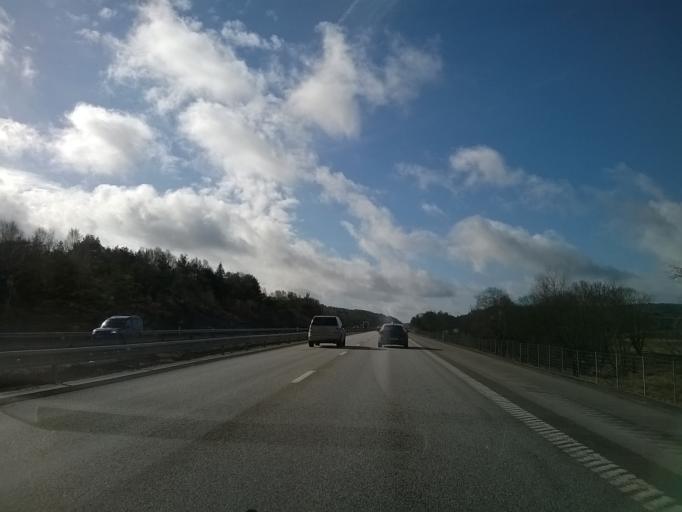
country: SE
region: Vaestra Goetaland
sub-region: Molndal
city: Lindome
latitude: 57.5433
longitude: 12.0524
